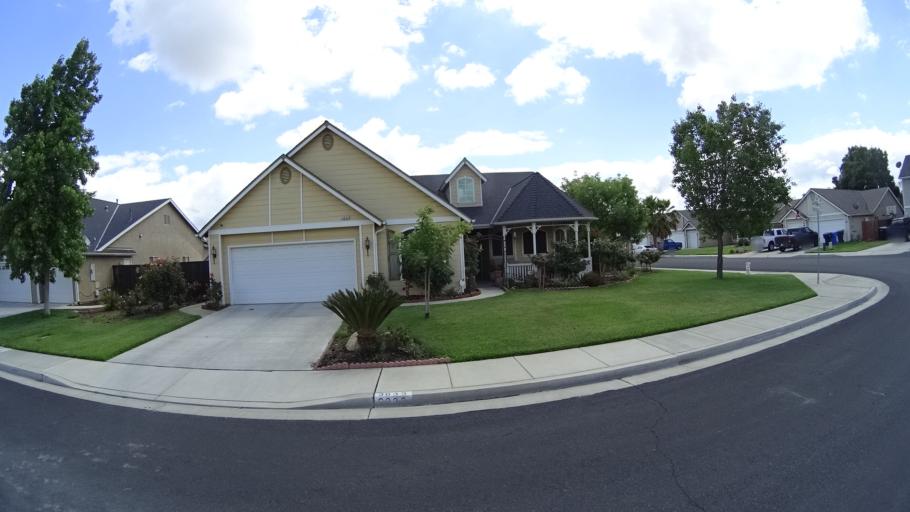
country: US
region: California
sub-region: Kings County
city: Lucerne
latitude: 36.3652
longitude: -119.6632
